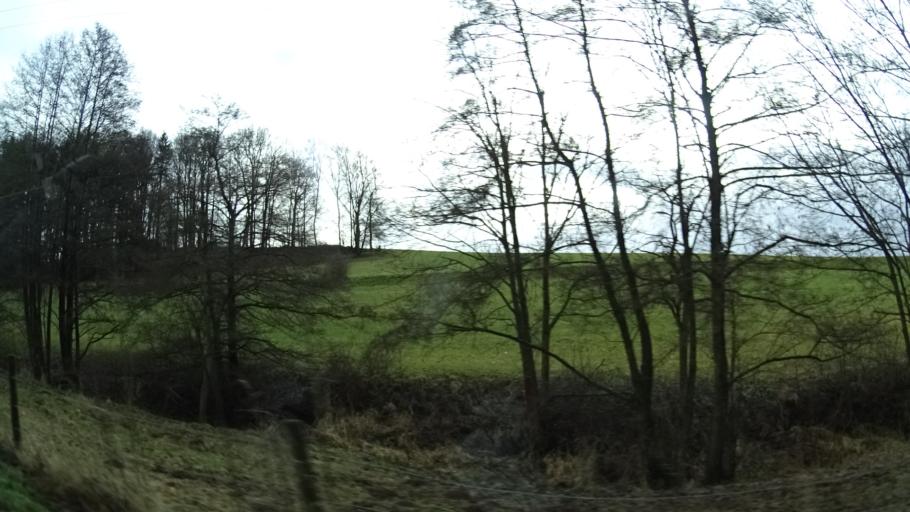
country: DE
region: Hesse
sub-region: Regierungsbezirk Kassel
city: Hilders
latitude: 50.6154
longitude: 9.9347
